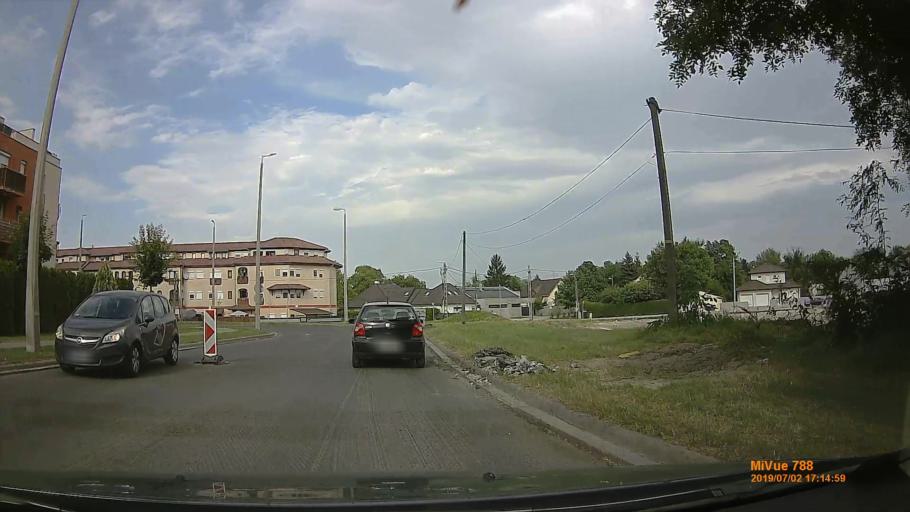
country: HU
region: Gyor-Moson-Sopron
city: Mosonmagyarovar
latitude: 47.8642
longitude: 17.2796
